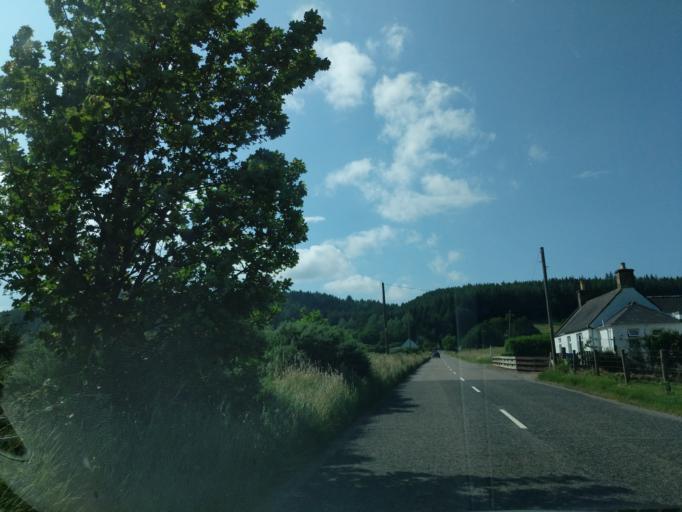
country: GB
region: Scotland
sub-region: Moray
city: Rothes
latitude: 57.5526
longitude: -3.1481
